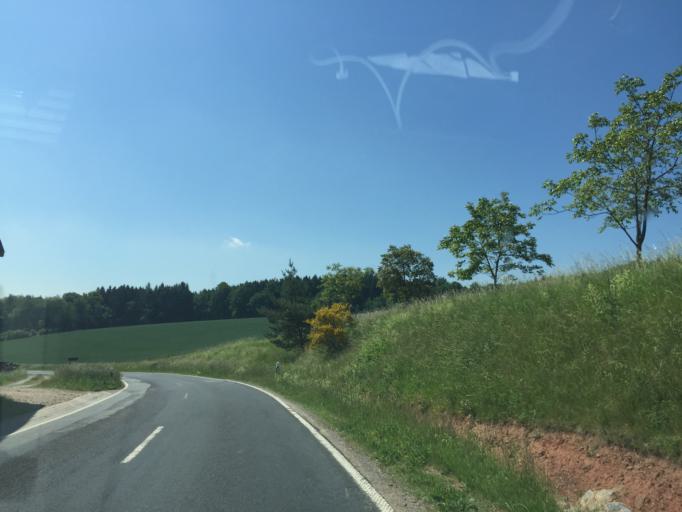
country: DE
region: Bavaria
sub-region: Regierungsbezirk Unterfranken
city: Eichenbuhl
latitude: 49.6585
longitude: 9.3064
